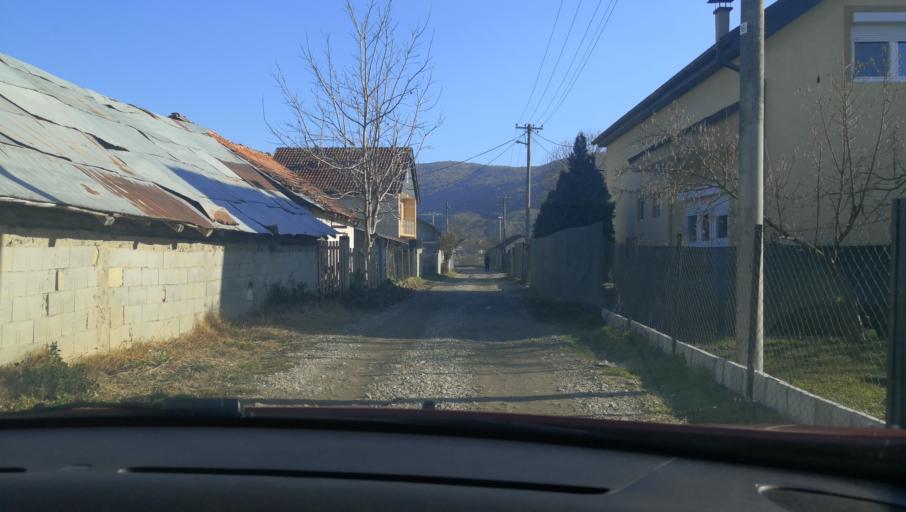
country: MK
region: Tetovo
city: Pirok
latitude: 41.9031
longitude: 20.9596
